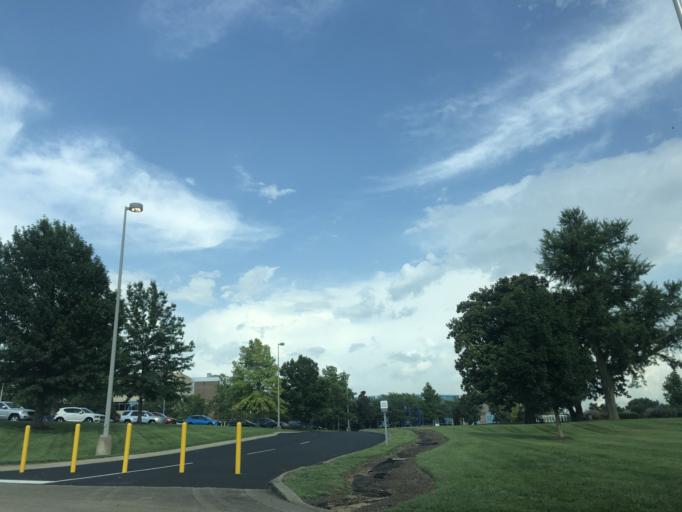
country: US
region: Tennessee
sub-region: Davidson County
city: Oak Hill
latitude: 36.1043
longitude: -86.6799
